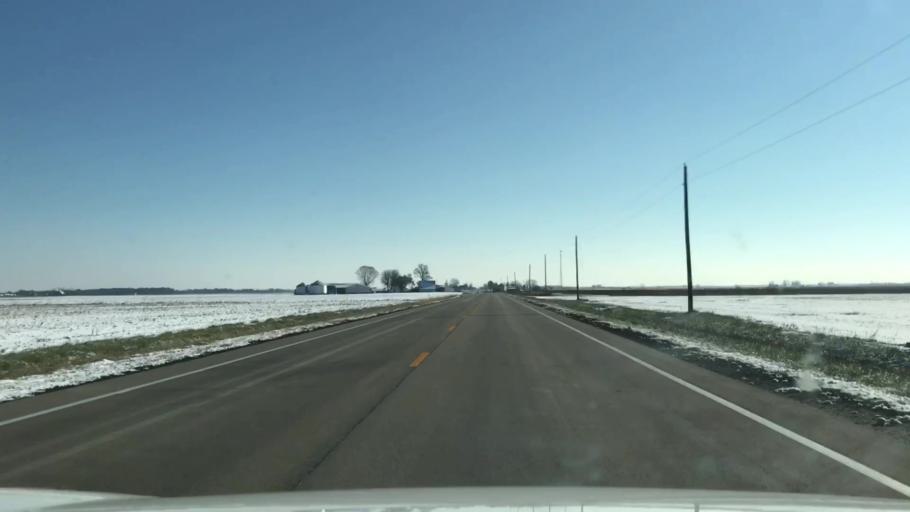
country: US
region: Illinois
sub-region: Washington County
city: Okawville
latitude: 38.4428
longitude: -89.5160
